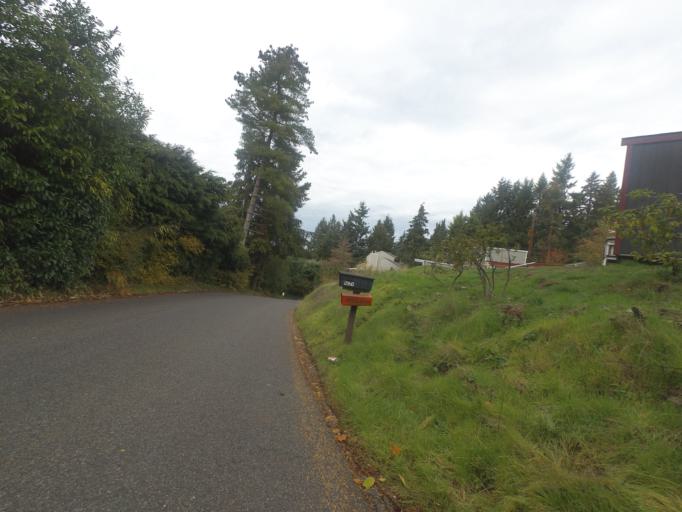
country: US
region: Washington
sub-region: Pierce County
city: University Place
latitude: 47.2165
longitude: -122.5682
